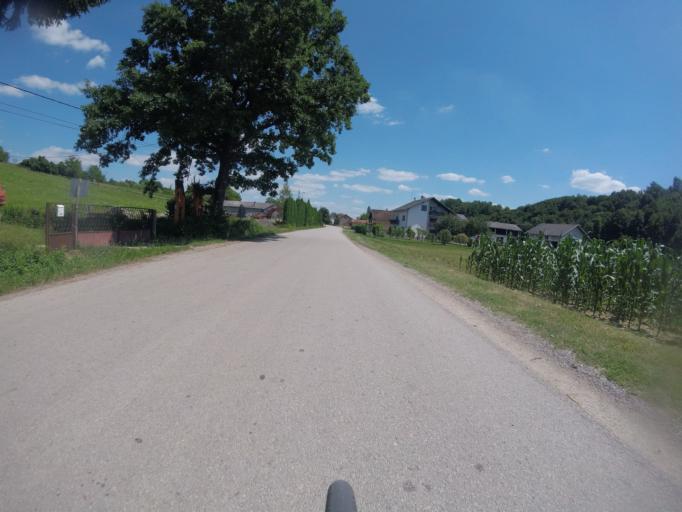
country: HR
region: Karlovacka
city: Ozalj
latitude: 45.6576
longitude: 15.5070
